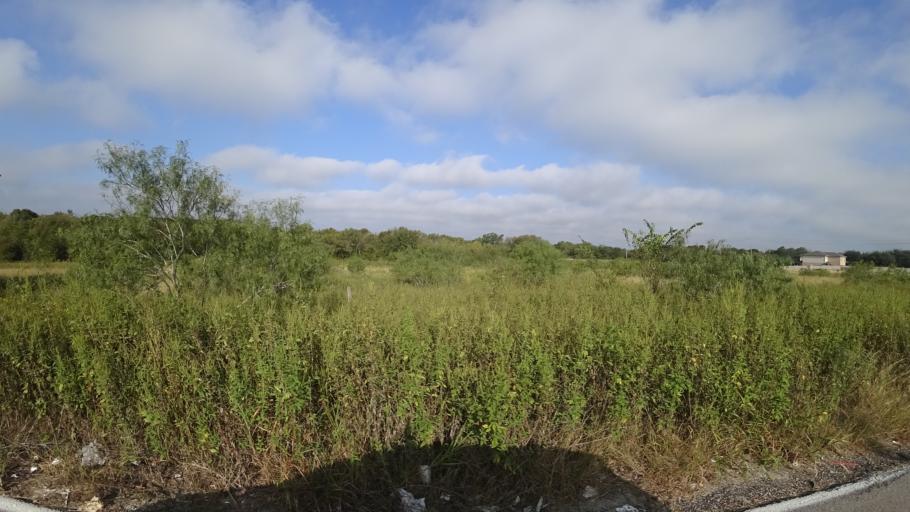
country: US
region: Texas
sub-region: Travis County
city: Manor
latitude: 30.3678
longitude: -97.6151
